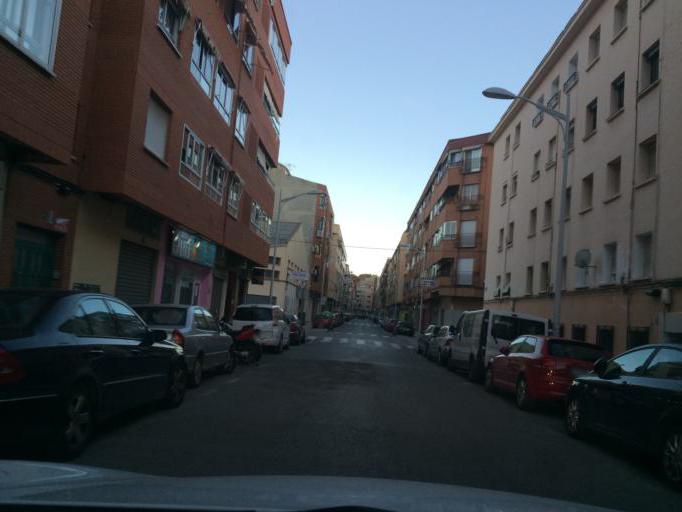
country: ES
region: Castille-La Mancha
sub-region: Provincia de Albacete
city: Albacete
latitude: 39.0037
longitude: -1.8624
